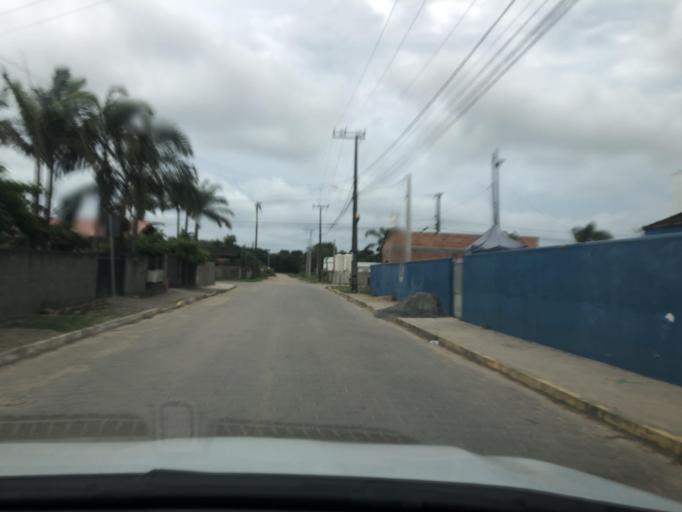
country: BR
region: Santa Catarina
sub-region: Sao Francisco Do Sul
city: Sao Francisco do Sul
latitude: -26.2346
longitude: -48.5236
